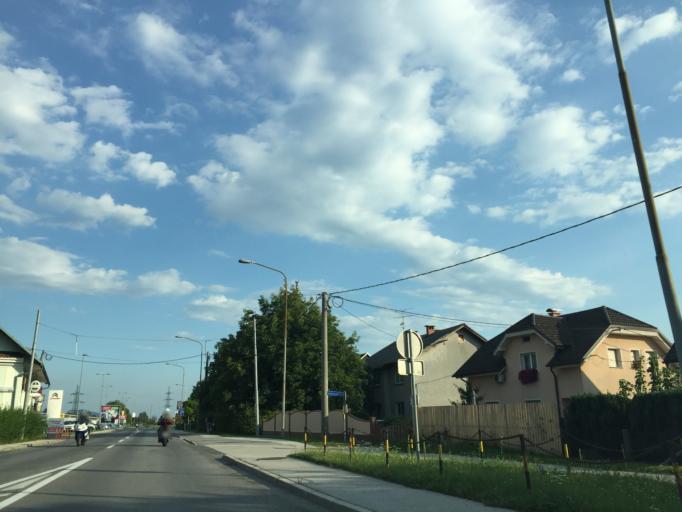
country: SI
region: Kranj
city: Kranj
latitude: 46.2310
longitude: 14.3536
